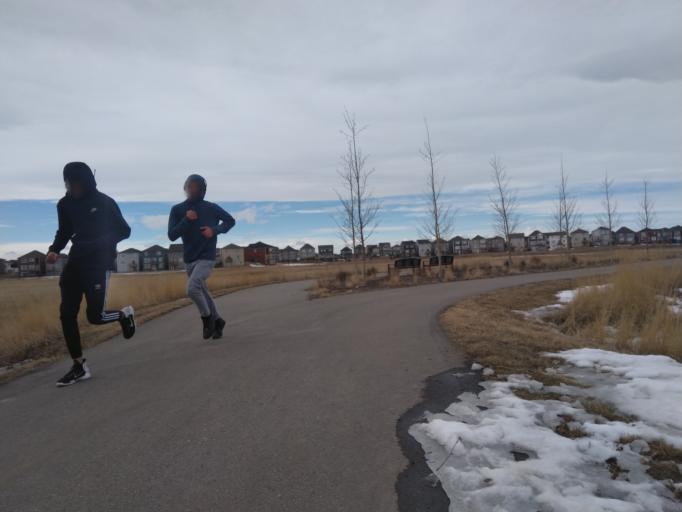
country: CA
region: Alberta
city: Calgary
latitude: 51.1489
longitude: -113.9569
